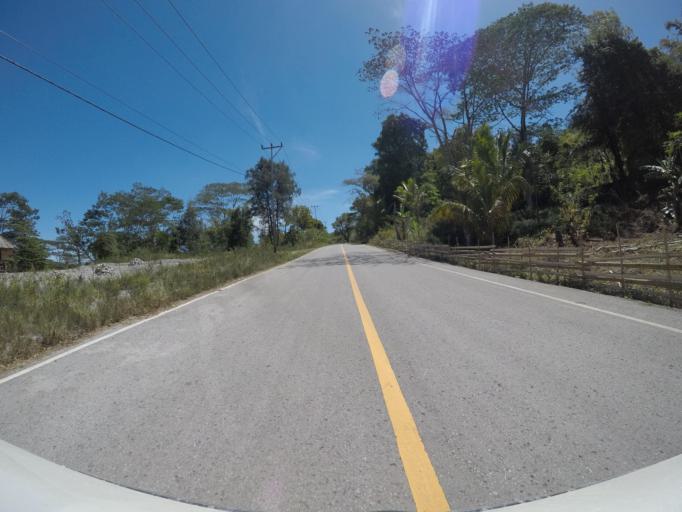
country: TL
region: Manatuto
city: Manatuto
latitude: -8.7863
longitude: 125.9690
